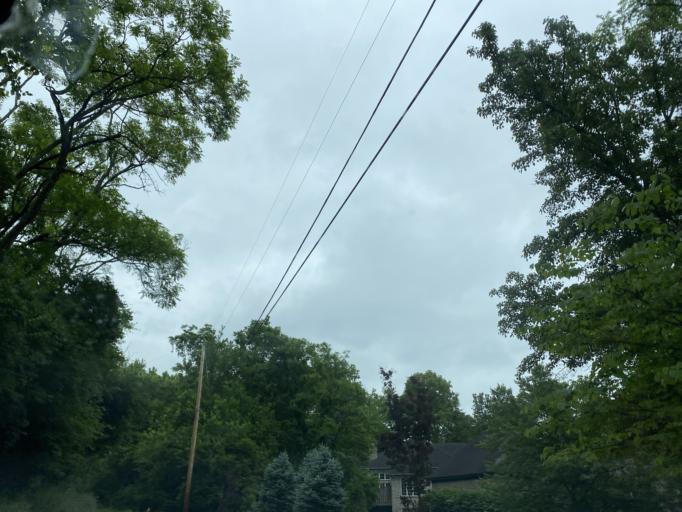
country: US
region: Kentucky
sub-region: Campbell County
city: Dayton
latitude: 39.1011
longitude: -84.4563
